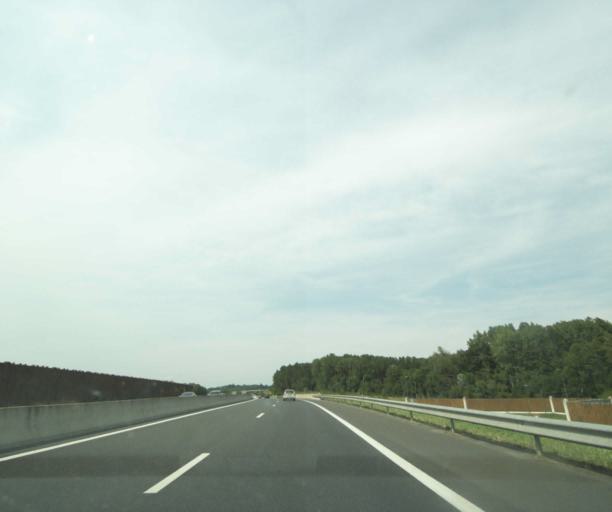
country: FR
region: Centre
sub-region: Departement d'Indre-et-Loire
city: La Membrolle-sur-Choisille
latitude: 47.4166
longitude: 0.6359
